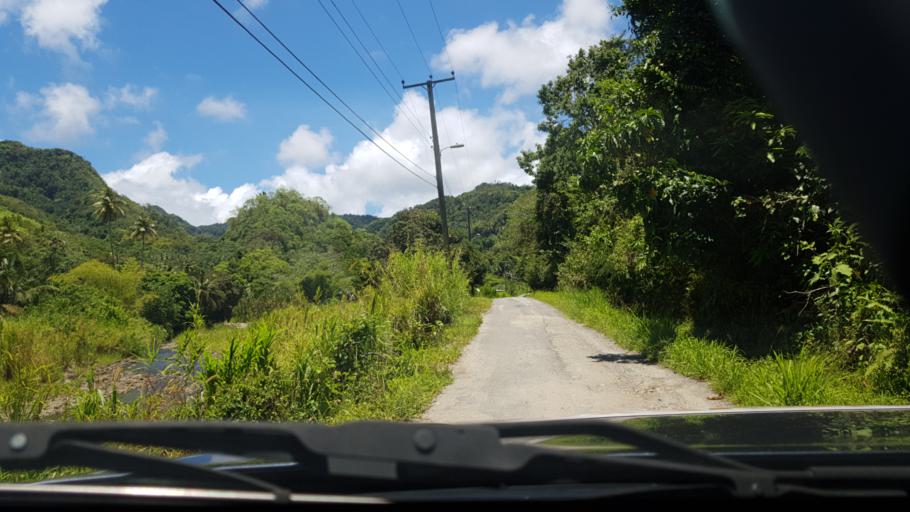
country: LC
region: Anse-la-Raye
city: Canaries
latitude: 13.9011
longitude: -61.0620
